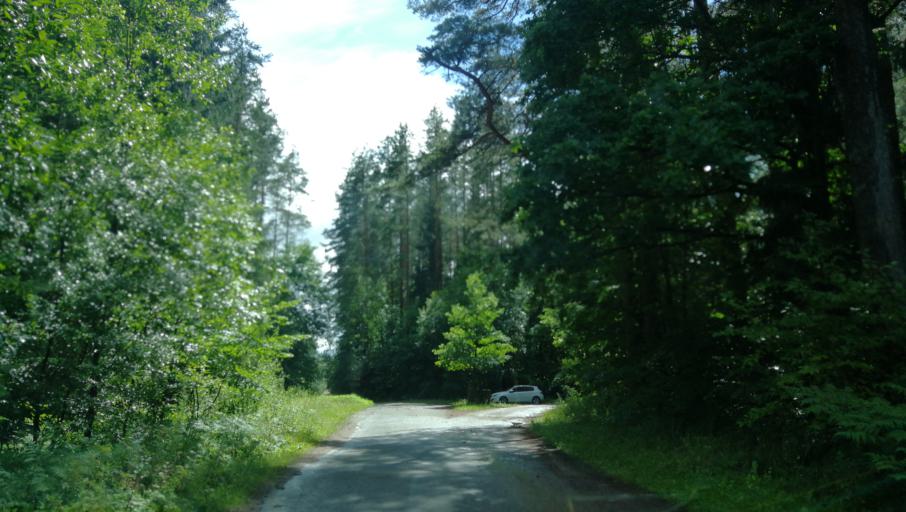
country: LV
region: Cesu Rajons
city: Cesis
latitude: 57.3108
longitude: 25.2191
